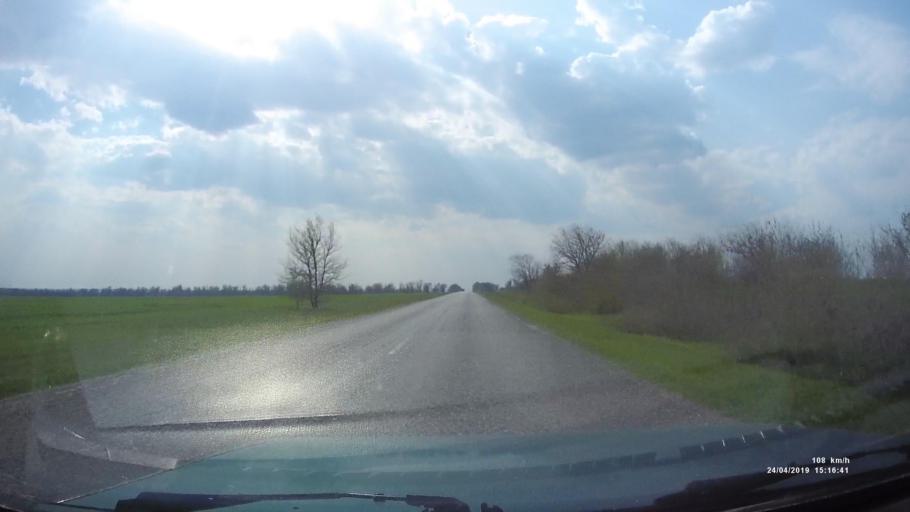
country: RU
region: Rostov
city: Remontnoye
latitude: 46.5464
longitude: 43.2051
